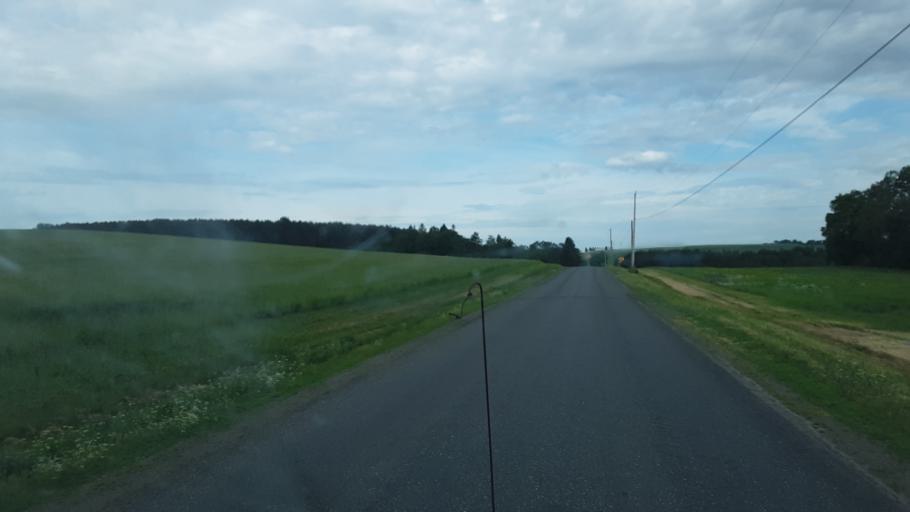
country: US
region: Maine
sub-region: Aroostook County
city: Caribou
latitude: 46.8112
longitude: -68.0172
